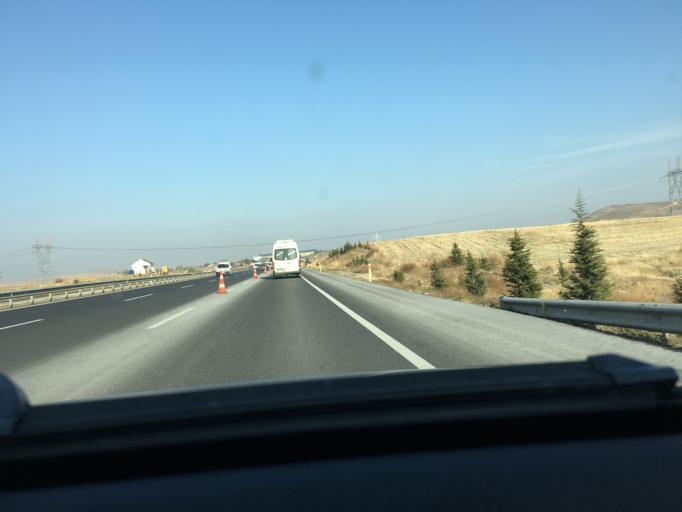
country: TR
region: Ankara
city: Temelli
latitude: 39.7094
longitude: 32.2866
